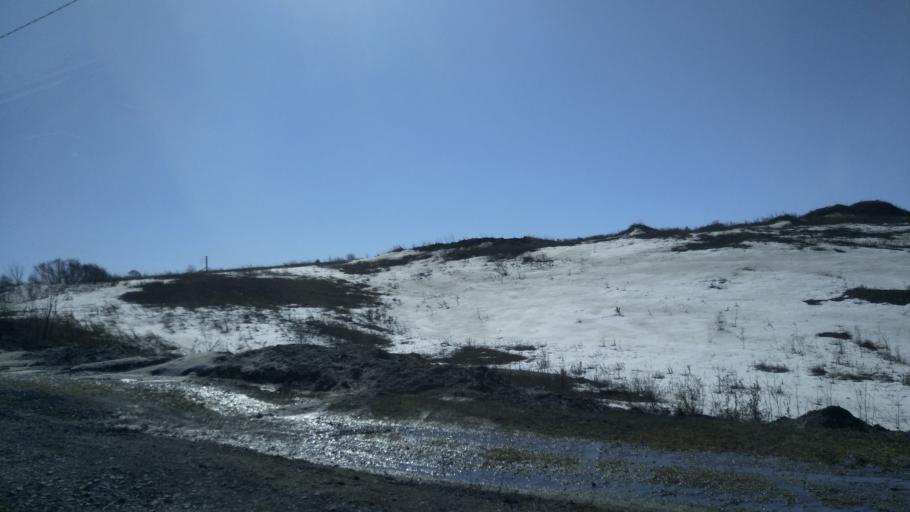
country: RU
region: Kemerovo
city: Yurga
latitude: 55.6990
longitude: 84.9601
